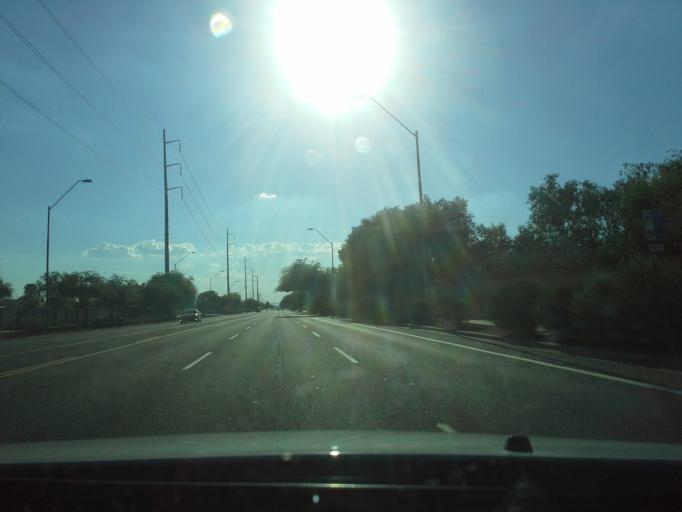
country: US
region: Arizona
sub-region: Maricopa County
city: Glendale
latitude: 33.6547
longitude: -112.1261
